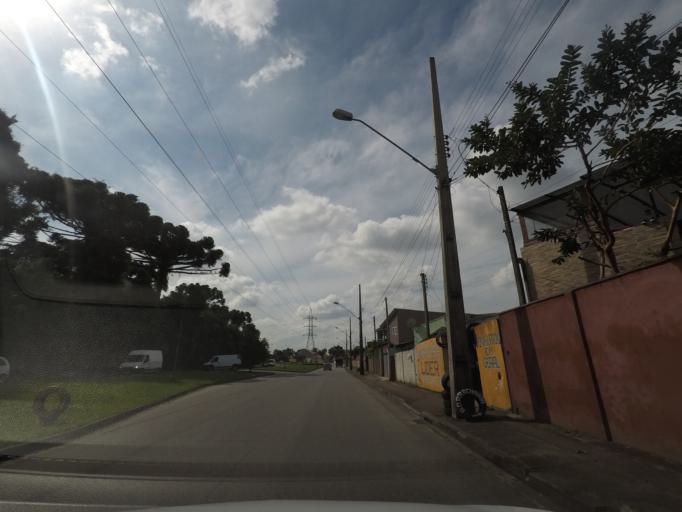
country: BR
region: Parana
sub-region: Sao Jose Dos Pinhais
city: Sao Jose dos Pinhais
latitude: -25.4911
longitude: -49.2071
